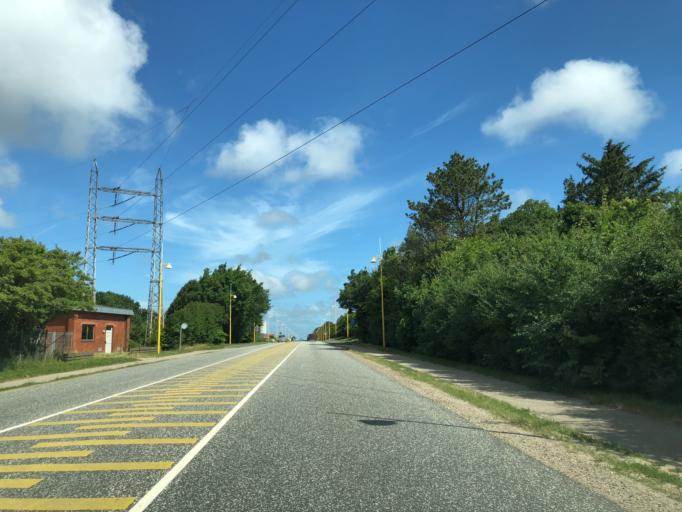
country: DK
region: Central Jutland
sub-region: Struer Kommune
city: Struer
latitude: 56.4824
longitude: 8.5835
